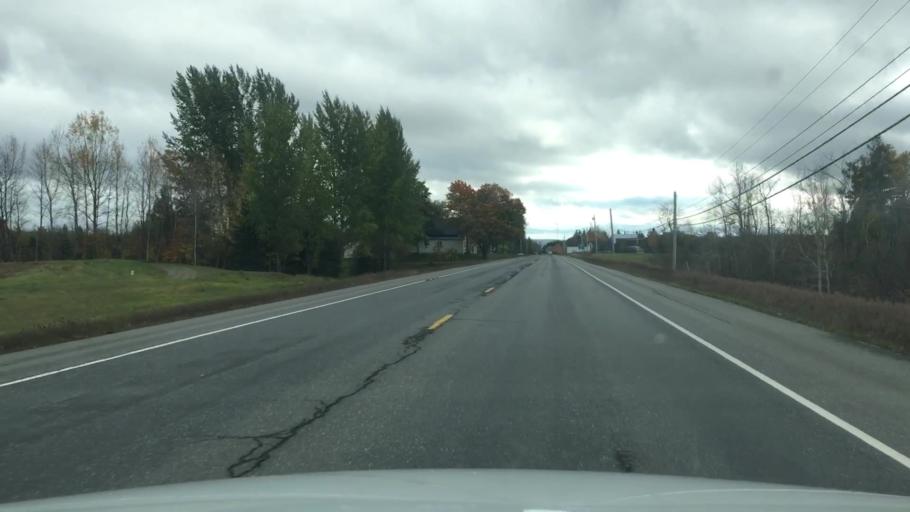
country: US
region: Maine
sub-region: Aroostook County
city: Houlton
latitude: 46.1823
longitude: -67.8411
